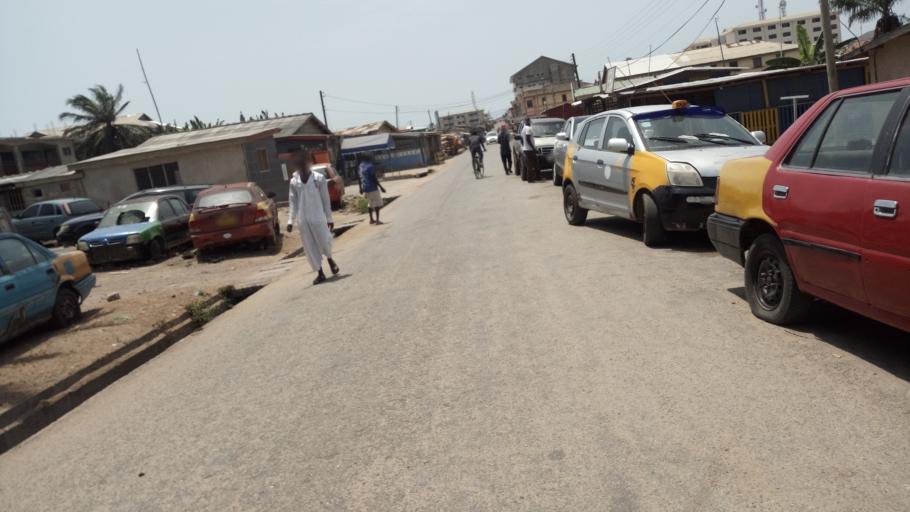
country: GH
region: Central
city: Winneba
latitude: 5.3477
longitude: -0.6273
